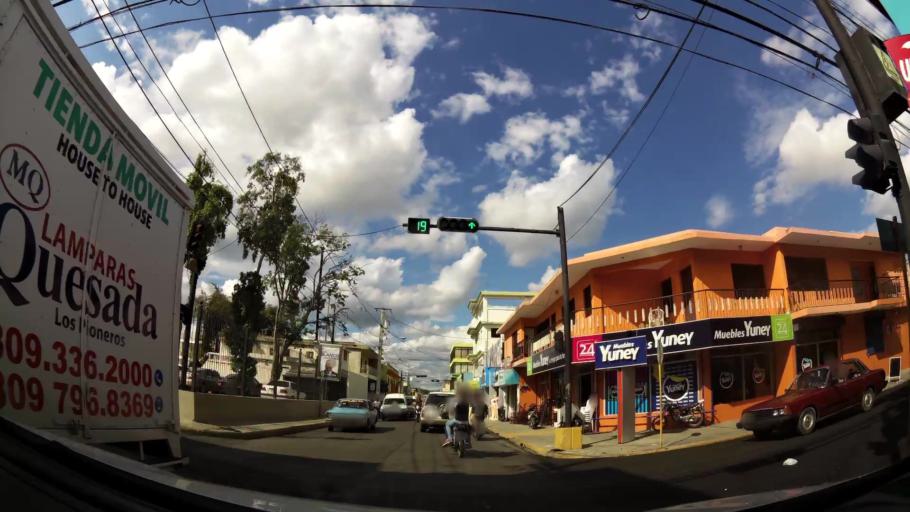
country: DO
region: La Vega
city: Concepcion de La Vega
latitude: 19.2258
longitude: -70.5319
